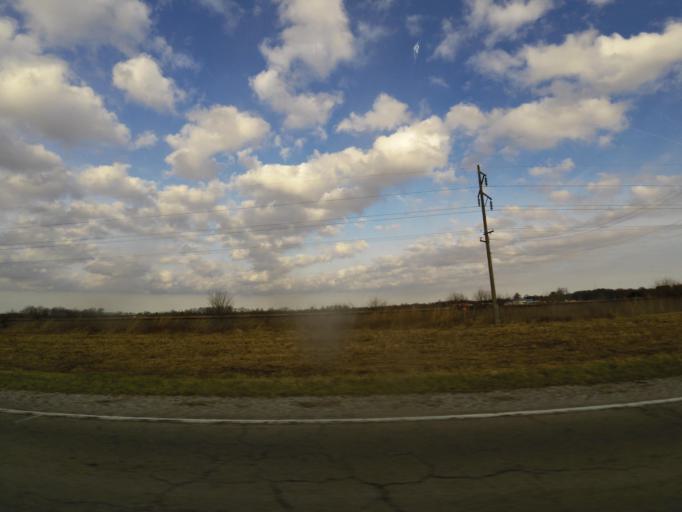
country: US
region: Illinois
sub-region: Bond County
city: Greenville
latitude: 38.9168
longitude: -89.2898
